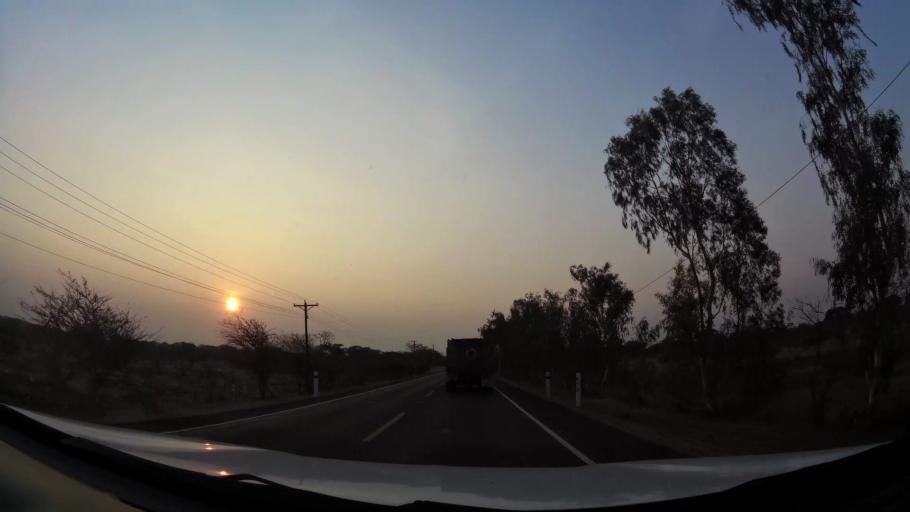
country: NI
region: Leon
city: La Paz Centro
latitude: 12.3053
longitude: -86.7778
